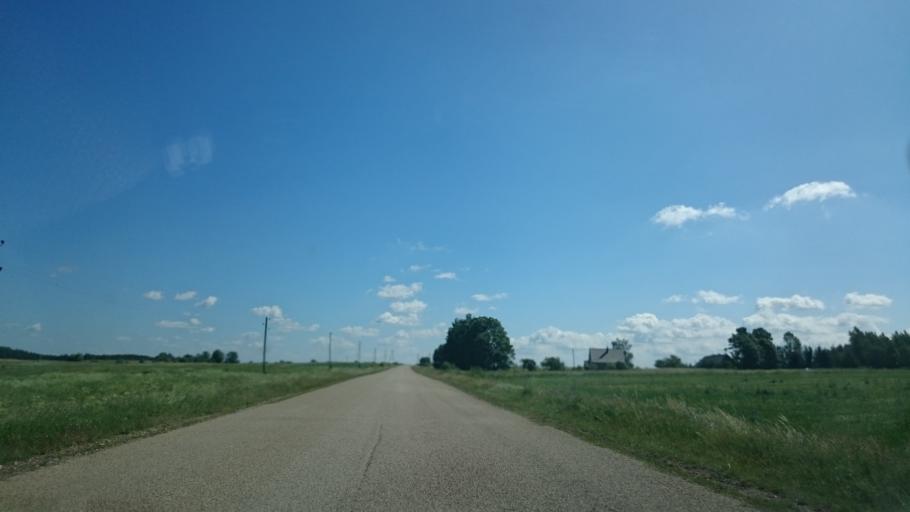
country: LV
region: Cibla
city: Cibla
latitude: 56.5333
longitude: 27.8465
